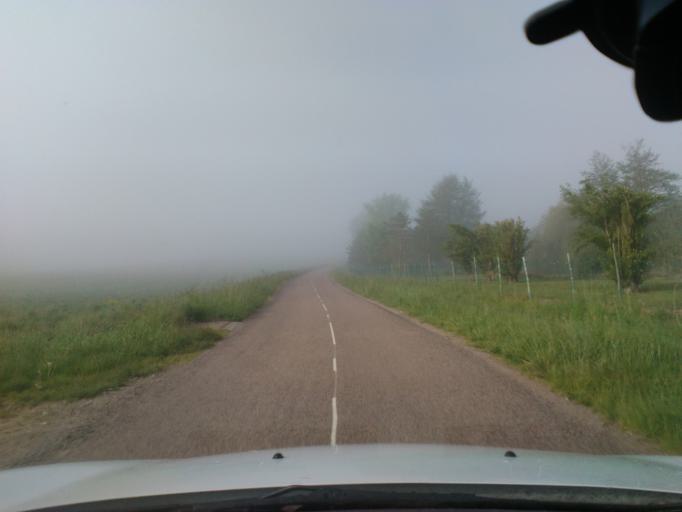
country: FR
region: Lorraine
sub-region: Departement des Vosges
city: Charmes
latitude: 48.3485
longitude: 6.2404
